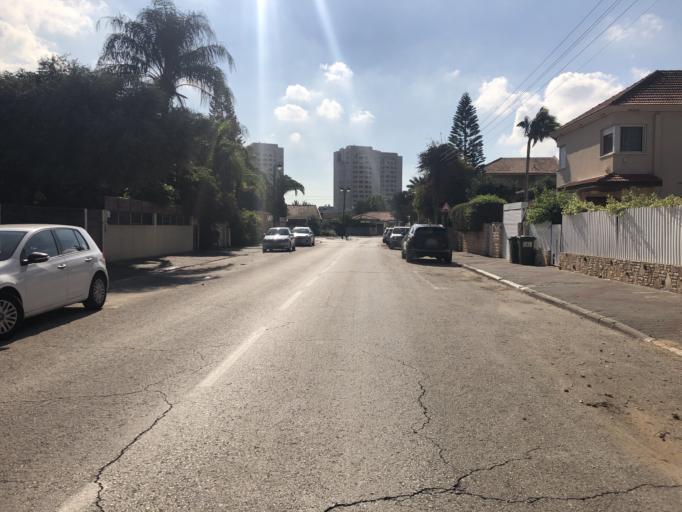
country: IL
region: Tel Aviv
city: Or Yehuda
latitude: 32.0300
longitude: 34.8693
